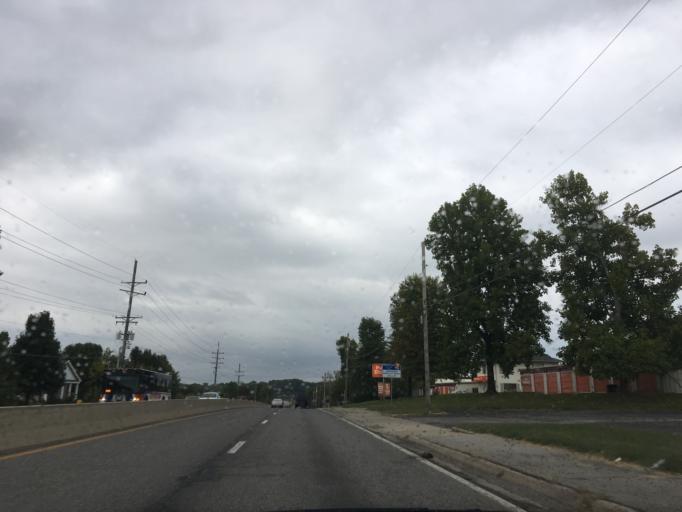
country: US
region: Missouri
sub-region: Saint Louis County
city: Maryland Heights
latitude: 38.7154
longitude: -90.4081
